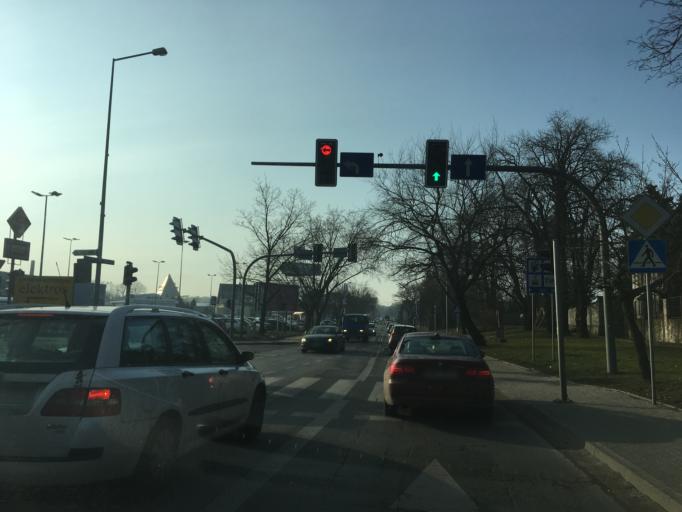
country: PL
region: Lower Silesian Voivodeship
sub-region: Powiat boleslawiecki
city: Boleslawiec
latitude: 51.2651
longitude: 15.5533
